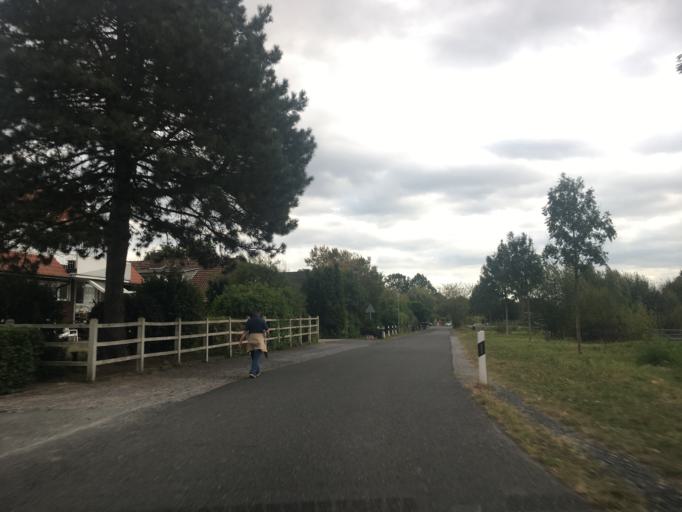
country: DE
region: North Rhine-Westphalia
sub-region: Regierungsbezirk Munster
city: Muenster
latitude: 51.9571
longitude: 7.5659
